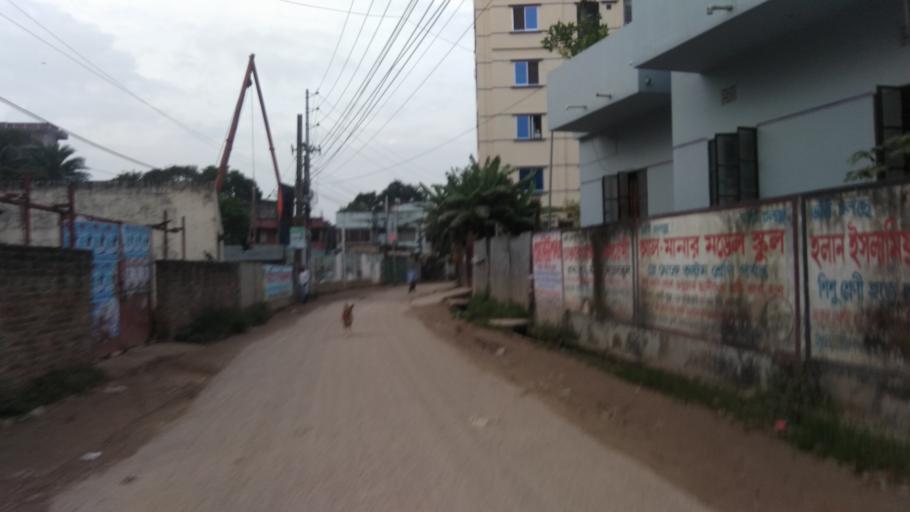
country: BD
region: Dhaka
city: Tungi
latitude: 23.8546
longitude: 90.4269
